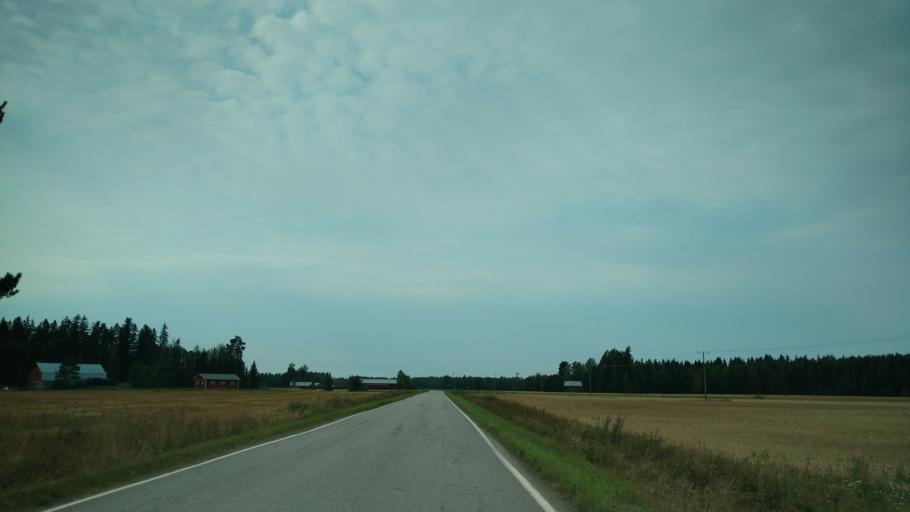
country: FI
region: Varsinais-Suomi
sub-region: Loimaa
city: Koski Tl
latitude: 60.7229
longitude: 23.1776
